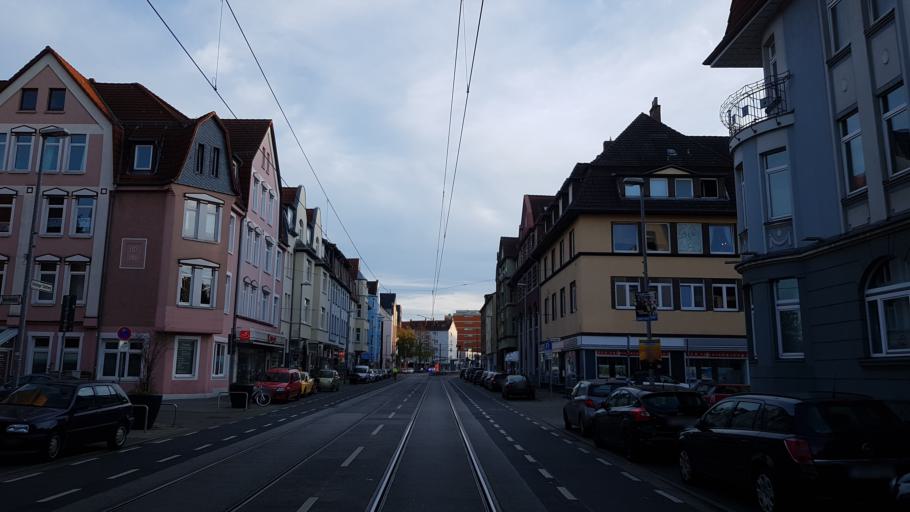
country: DE
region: Lower Saxony
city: Hannover
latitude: 52.3452
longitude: 9.7246
